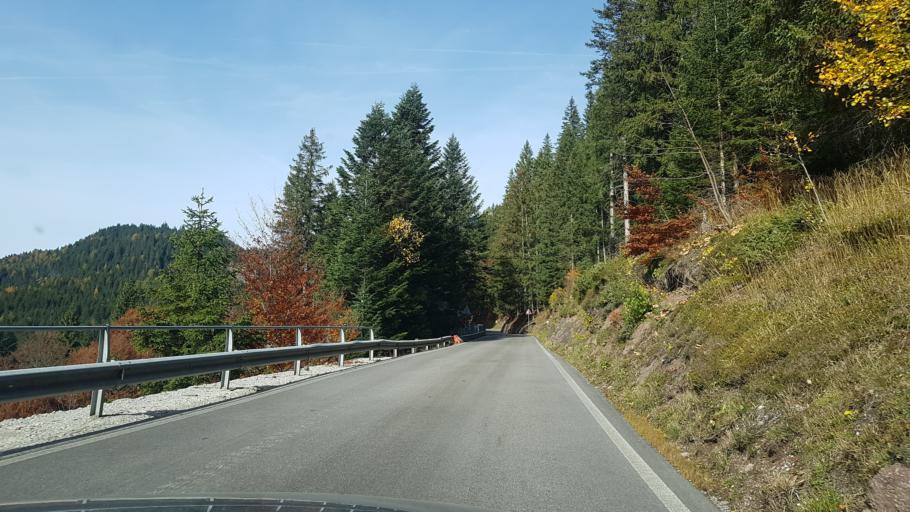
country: IT
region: Veneto
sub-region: Provincia di Belluno
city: Candide
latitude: 46.6464
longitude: 12.4515
